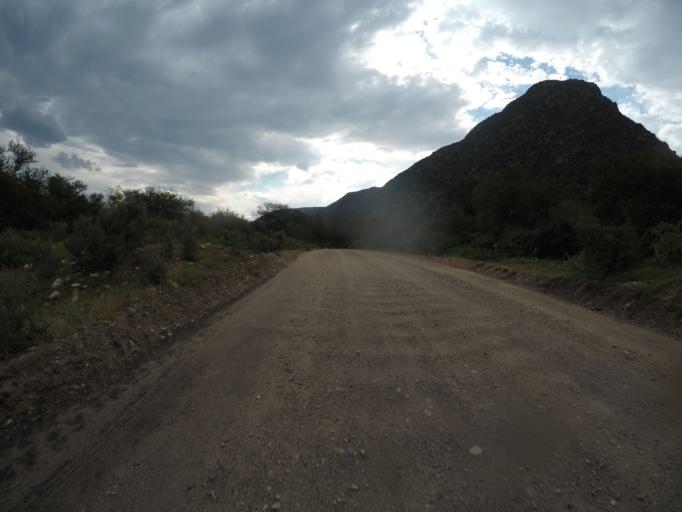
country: ZA
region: Eastern Cape
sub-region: Cacadu District Municipality
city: Kareedouw
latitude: -33.5776
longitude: 24.1452
